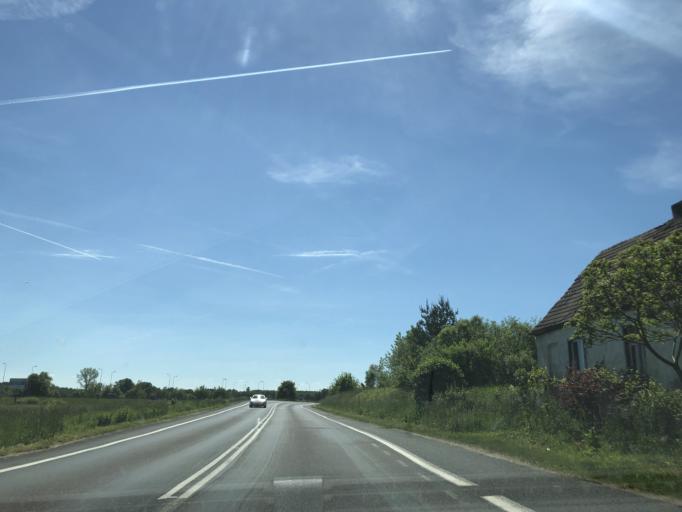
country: PL
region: West Pomeranian Voivodeship
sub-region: Powiat bialogardzki
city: Karlino
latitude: 54.0283
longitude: 15.8648
